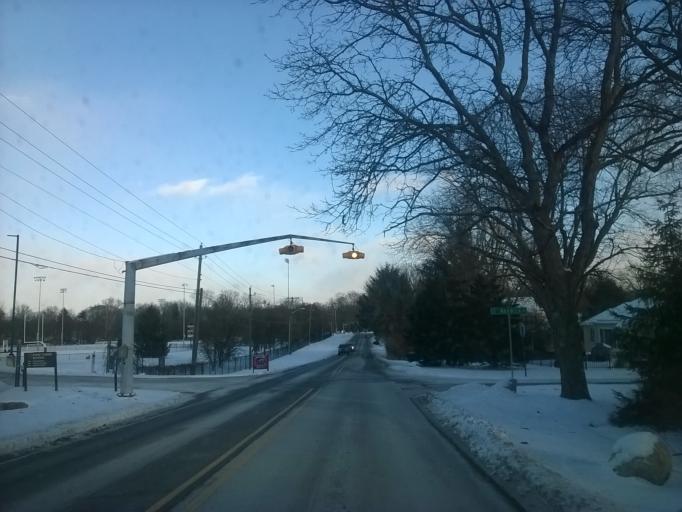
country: US
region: Indiana
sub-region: Marion County
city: Meridian Hills
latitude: 39.8832
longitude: -86.1496
